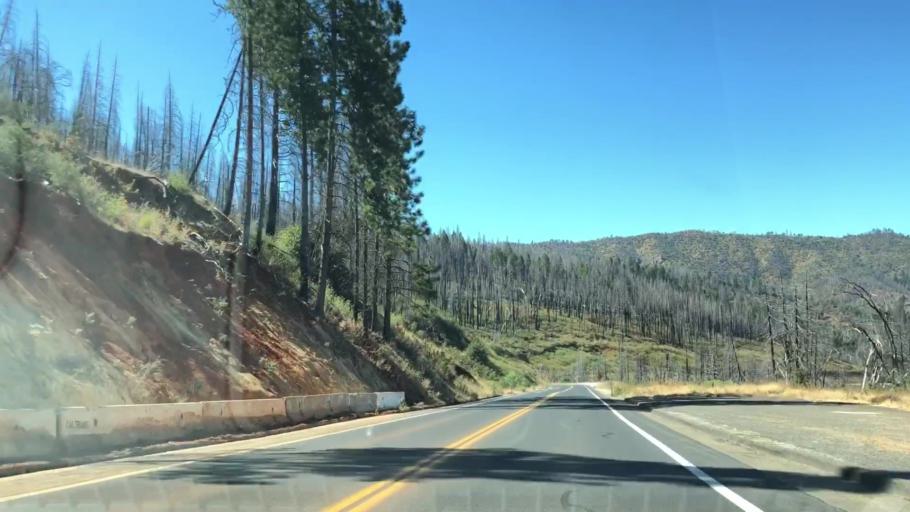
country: US
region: California
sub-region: Tuolumne County
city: Tuolumne City
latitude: 37.8277
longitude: -119.9852
